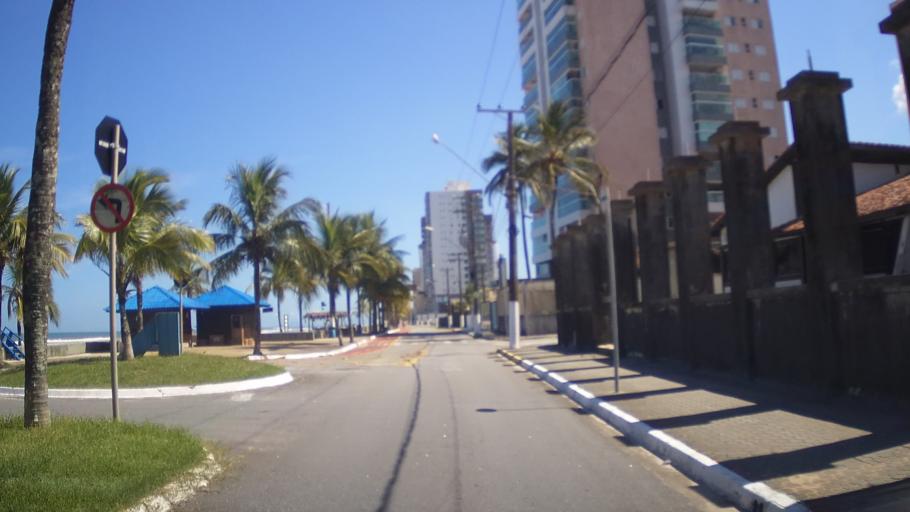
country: BR
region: Sao Paulo
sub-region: Mongagua
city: Mongagua
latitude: -24.0886
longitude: -46.6052
